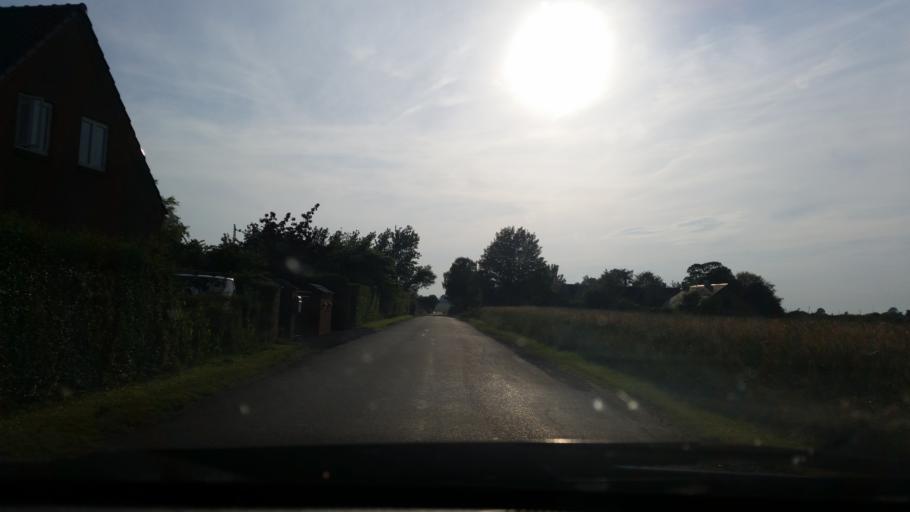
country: DK
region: Central Jutland
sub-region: Odder Kommune
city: Odder
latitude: 55.9062
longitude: 10.2191
